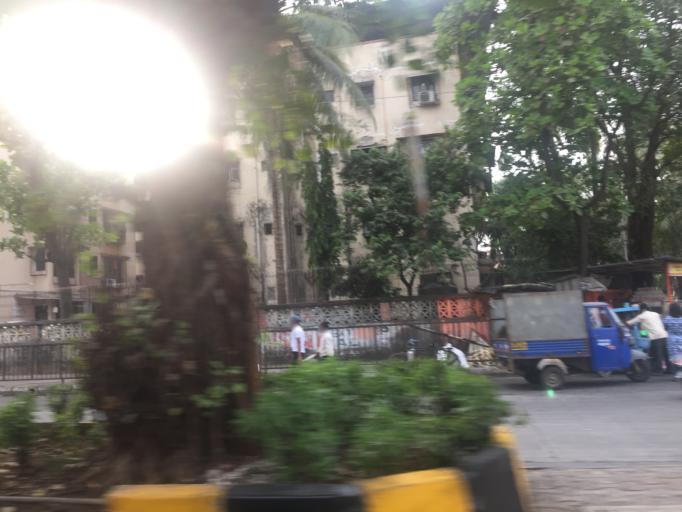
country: IN
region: Maharashtra
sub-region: Thane
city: Airoli
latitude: 19.1503
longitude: 72.9929
